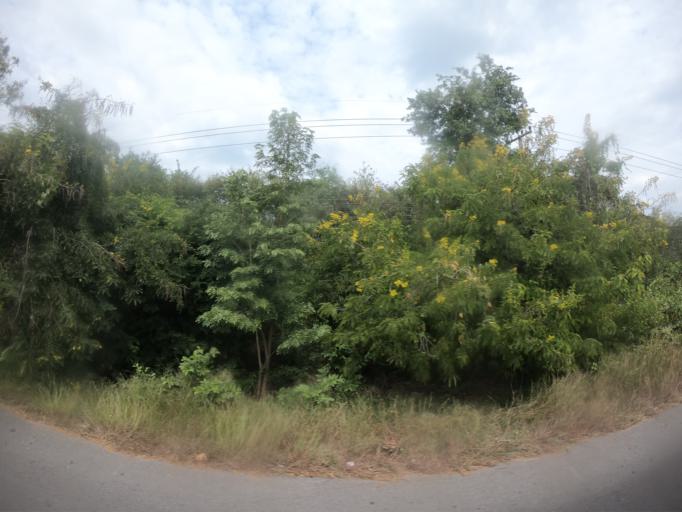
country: TH
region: Maha Sarakham
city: Maha Sarakham
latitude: 16.1611
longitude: 103.3522
